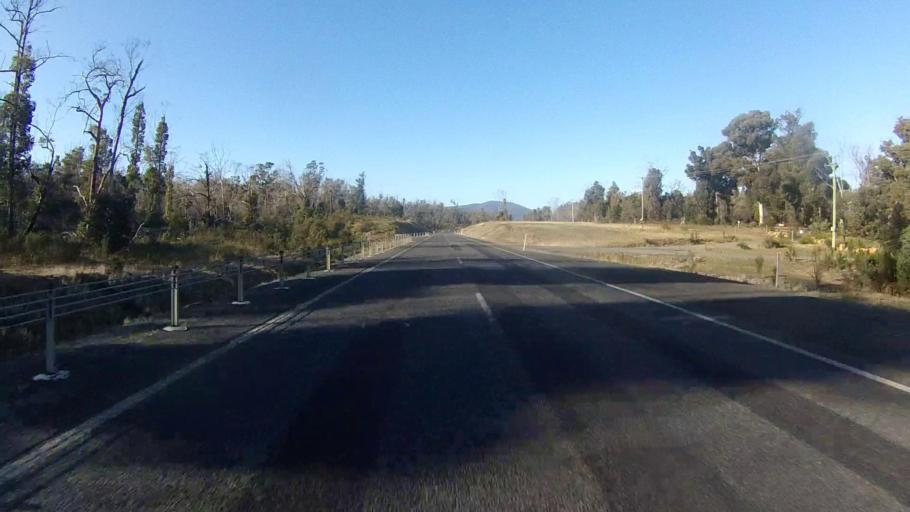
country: AU
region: Tasmania
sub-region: Sorell
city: Sorell
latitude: -42.9268
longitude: 147.8391
